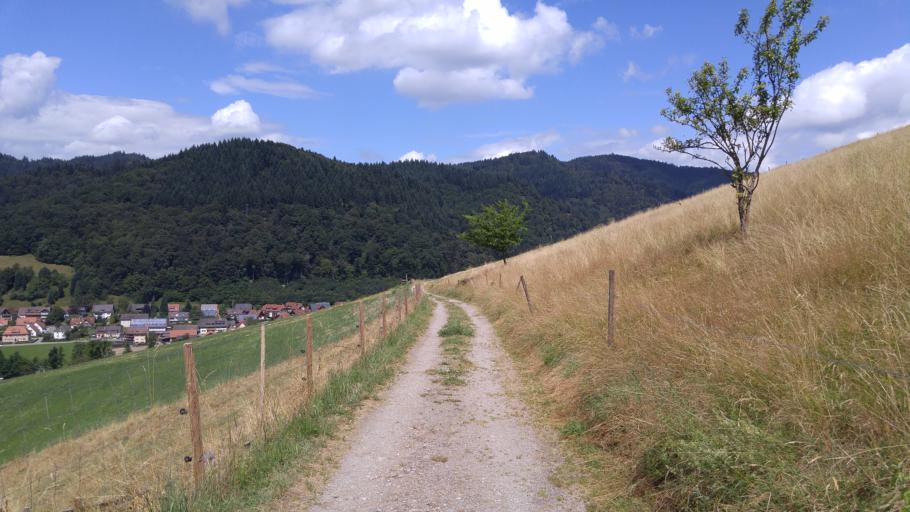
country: DE
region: Baden-Wuerttemberg
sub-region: Freiburg Region
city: Muenstertal/Schwarzwald
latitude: 47.8510
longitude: 7.7929
